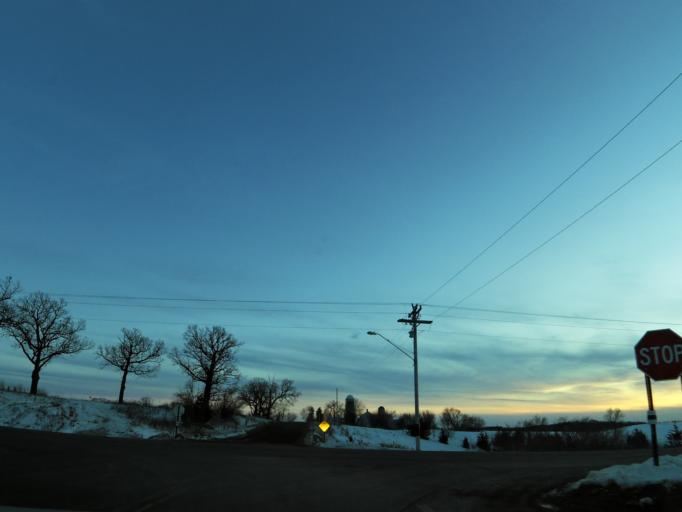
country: US
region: Minnesota
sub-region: Carver County
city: Chaska
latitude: 44.7327
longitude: -93.5622
